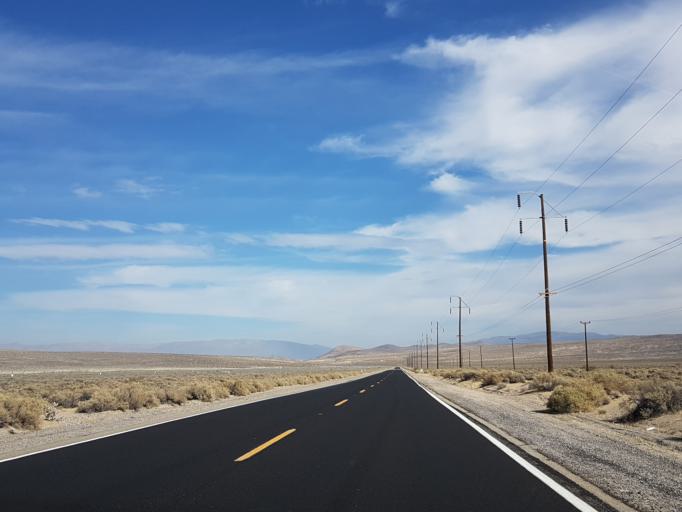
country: US
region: California
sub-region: San Bernardino County
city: Searles Valley
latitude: 35.6481
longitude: -117.4956
